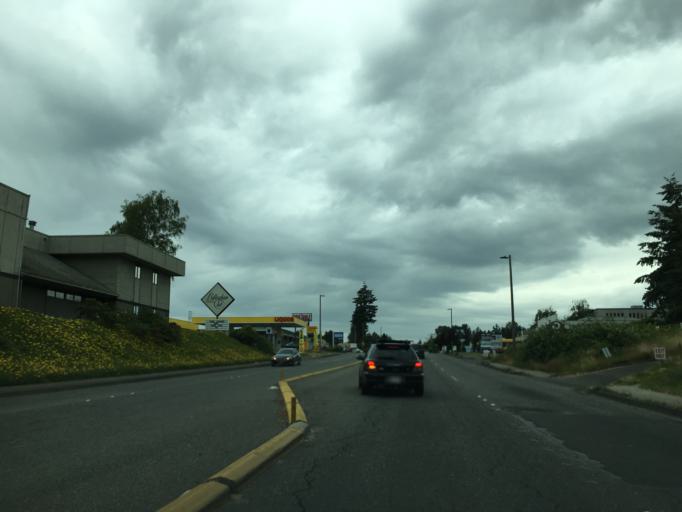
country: US
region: Washington
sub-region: Whatcom County
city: Bellingham
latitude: 48.7929
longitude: -122.4860
